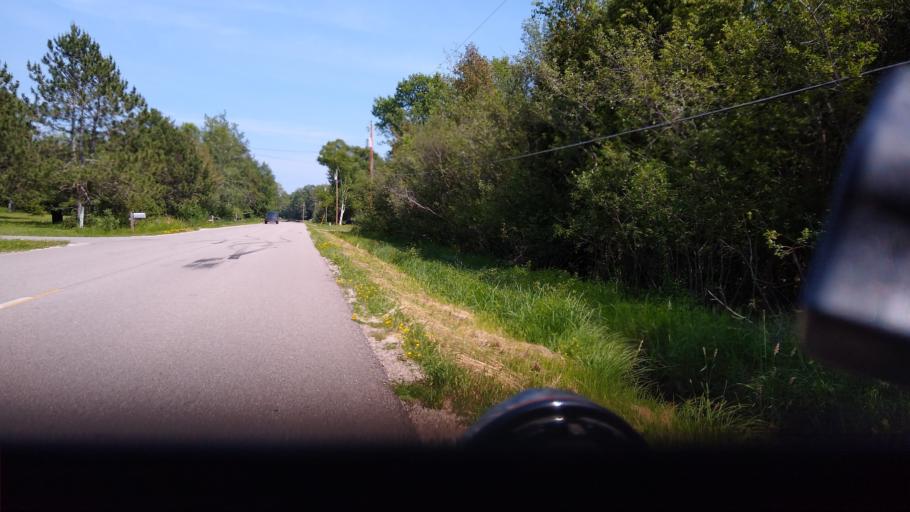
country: US
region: Michigan
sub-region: Delta County
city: Escanaba
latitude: 45.7100
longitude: -87.1058
